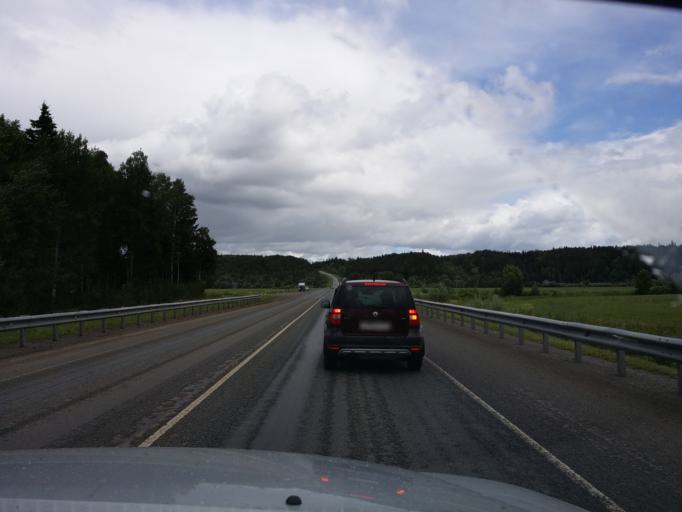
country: RU
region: Tjumen
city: Abalak
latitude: 58.4675
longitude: 68.5385
